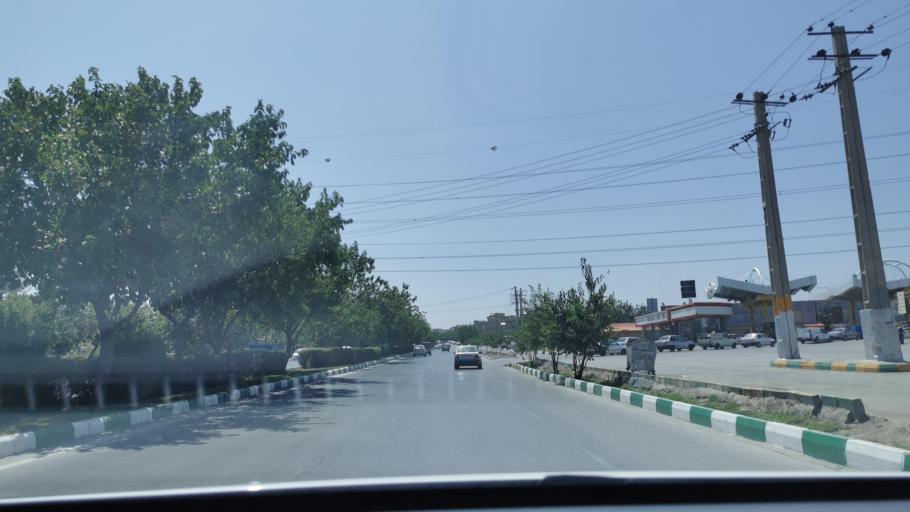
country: IR
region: Razavi Khorasan
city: Mashhad
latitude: 36.3506
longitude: 59.6295
